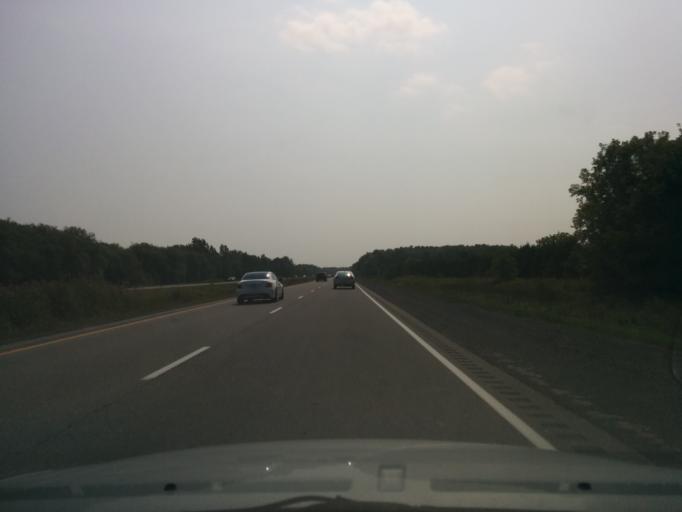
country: CA
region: Ontario
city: Bells Corners
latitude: 45.1725
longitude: -75.7007
